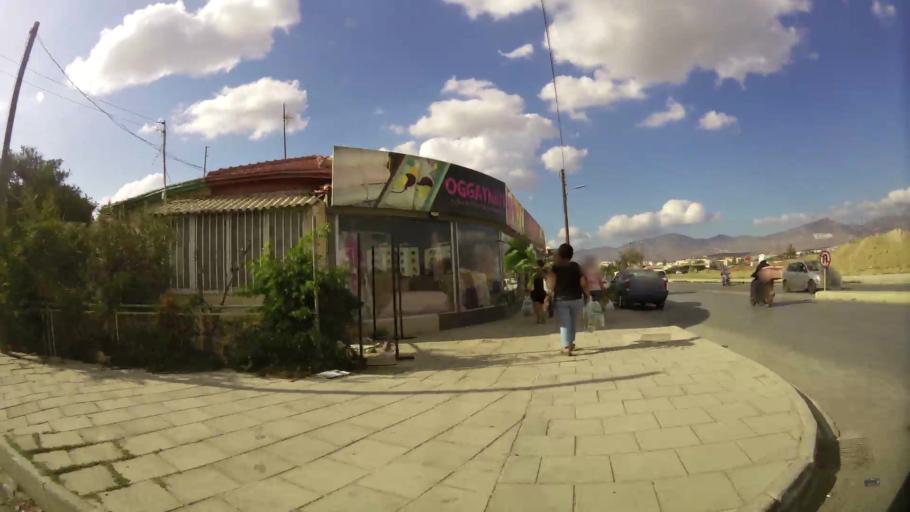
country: CY
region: Lefkosia
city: Nicosia
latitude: 35.1996
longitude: 33.3533
